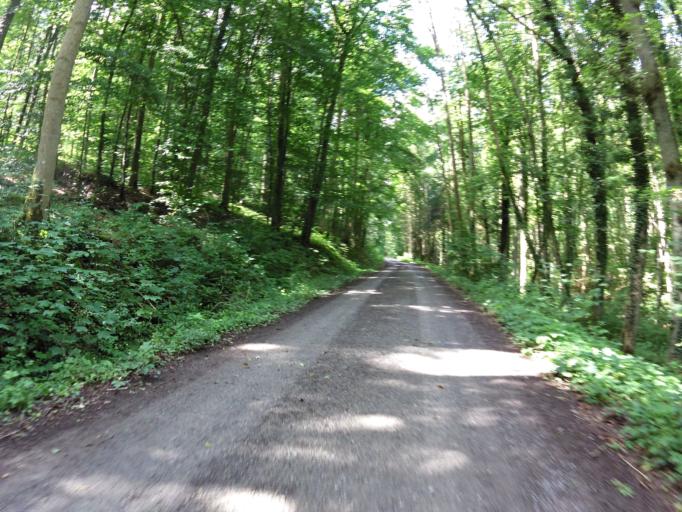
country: DE
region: Bavaria
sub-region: Regierungsbezirk Unterfranken
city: Margetshochheim
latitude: 49.8241
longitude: 9.8490
